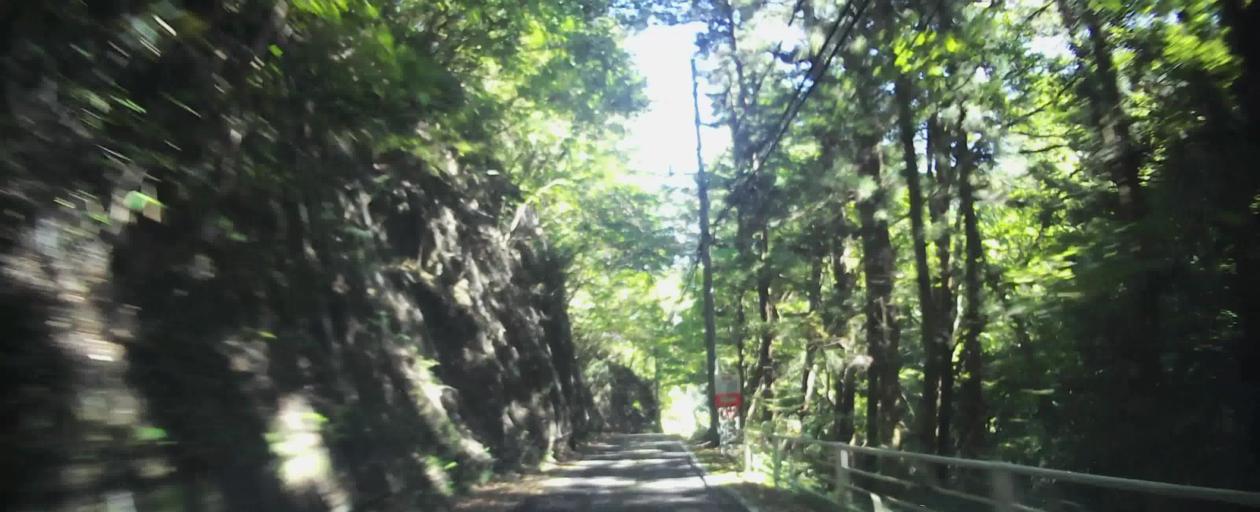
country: JP
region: Gunma
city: Nakanojomachi
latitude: 36.5758
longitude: 138.7326
